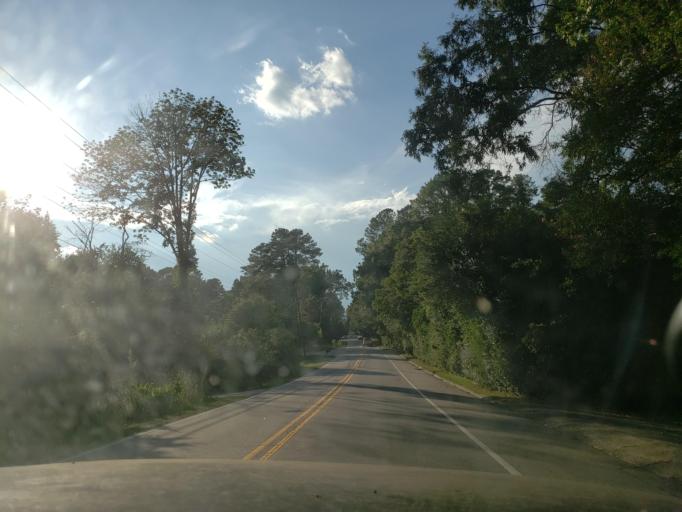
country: US
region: North Carolina
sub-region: Durham County
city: Durham
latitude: 35.9696
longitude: -78.9263
